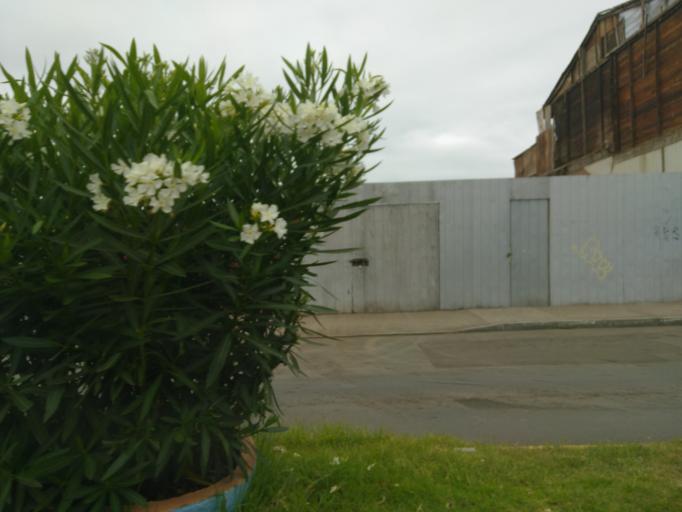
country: CL
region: Antofagasta
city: Taltal
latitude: -25.4058
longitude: -70.4831
